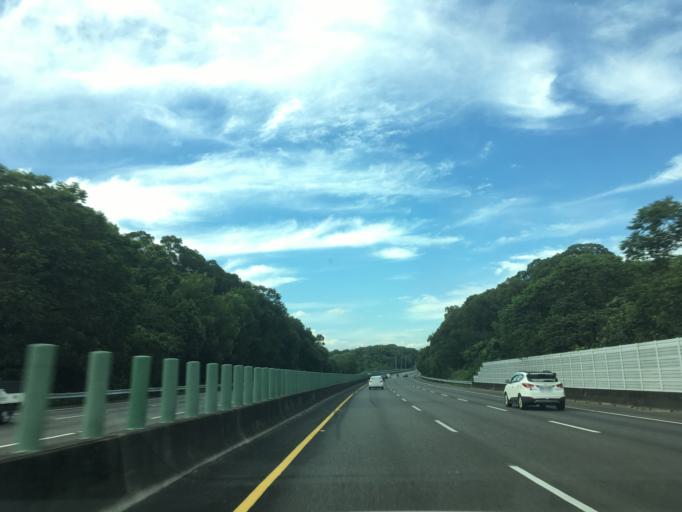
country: TW
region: Taiwan
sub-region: Chiayi
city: Jiayi Shi
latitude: 23.5700
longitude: 120.5056
